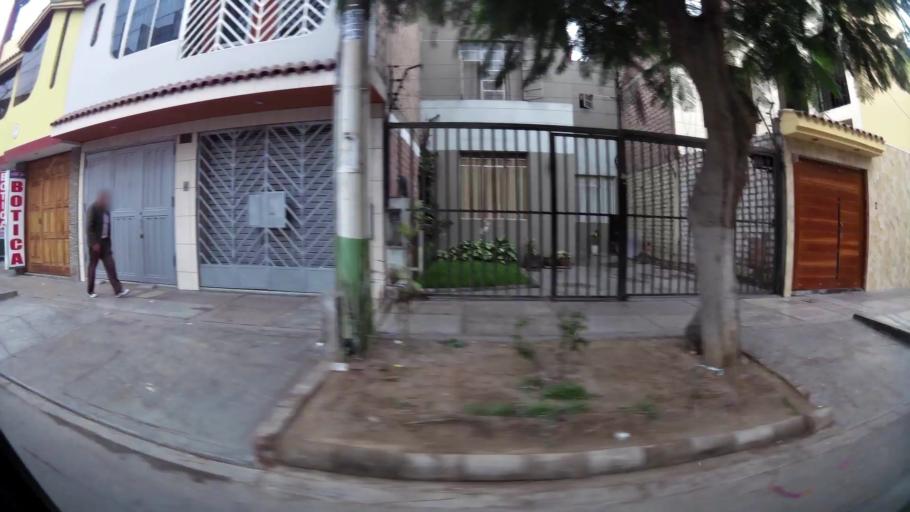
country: PE
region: Lima
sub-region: Lima
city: Independencia
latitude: -11.9667
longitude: -77.0706
